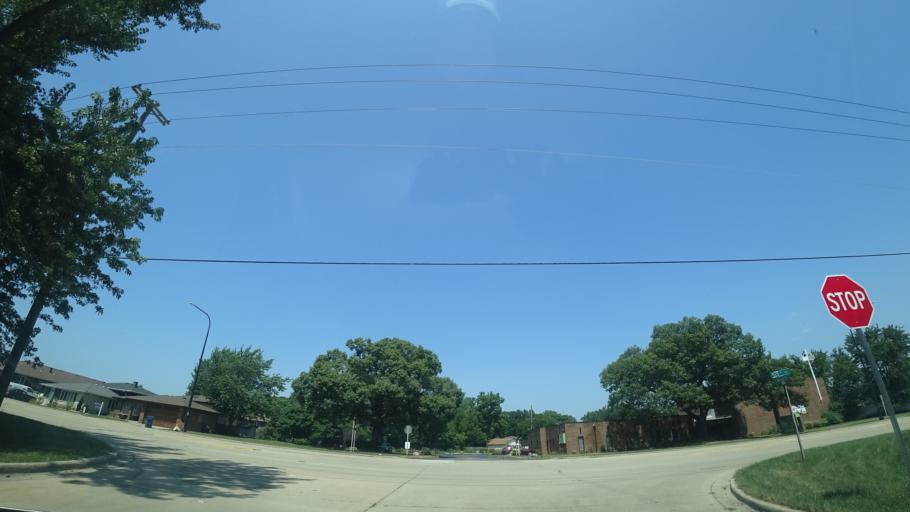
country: US
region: Illinois
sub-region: Cook County
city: Alsip
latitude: 41.6833
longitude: -87.7480
